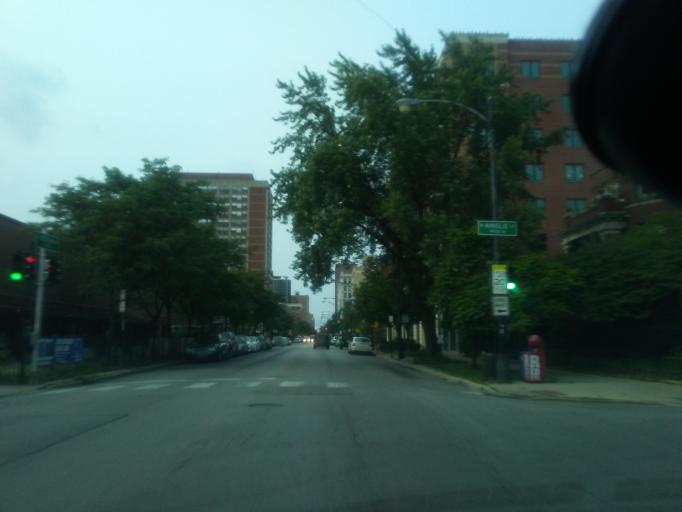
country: US
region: Illinois
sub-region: Cook County
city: Evanston
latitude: 41.9716
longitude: -87.6549
